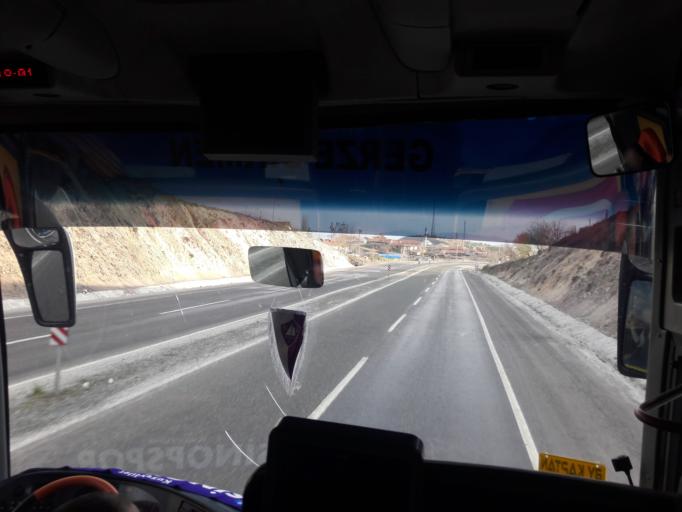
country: TR
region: Cankiri
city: Korgun
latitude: 40.7425
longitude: 33.5233
